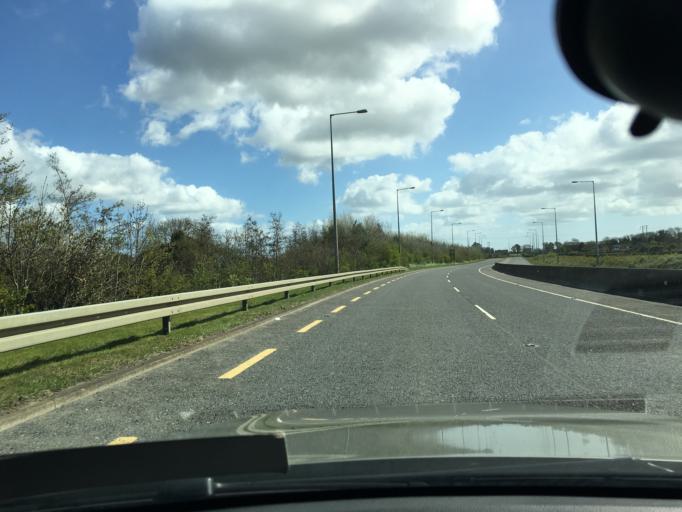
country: IE
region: Leinster
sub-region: Fingal County
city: Blanchardstown
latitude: 53.4348
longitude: -6.3402
